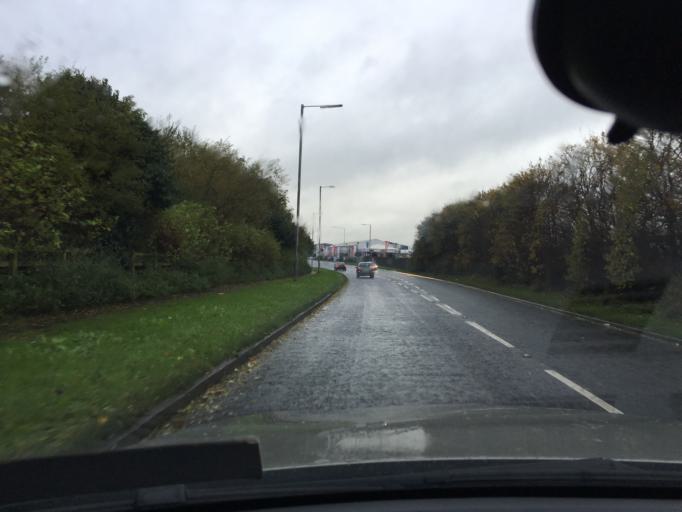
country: GB
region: Northern Ireland
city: Carnmoney
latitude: 54.6709
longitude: -5.9712
